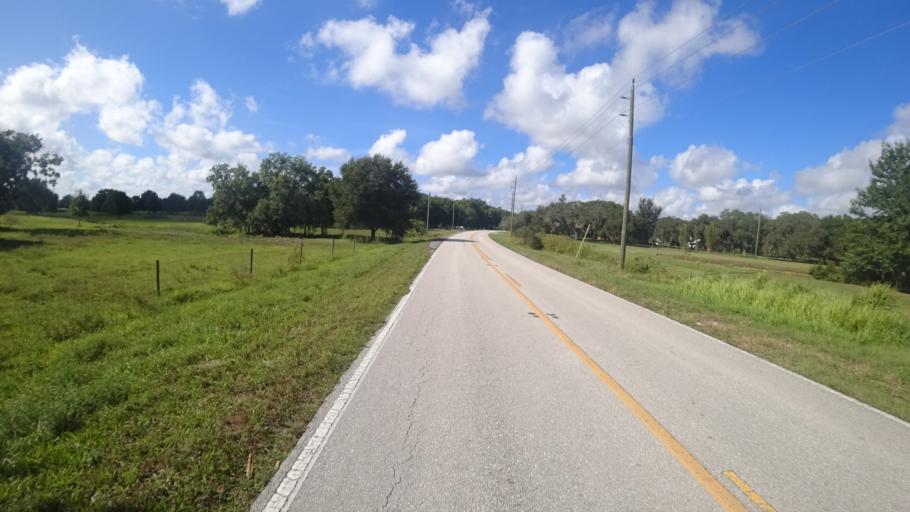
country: US
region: Florida
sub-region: Sarasota County
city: Lake Sarasota
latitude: 27.3514
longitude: -82.2383
